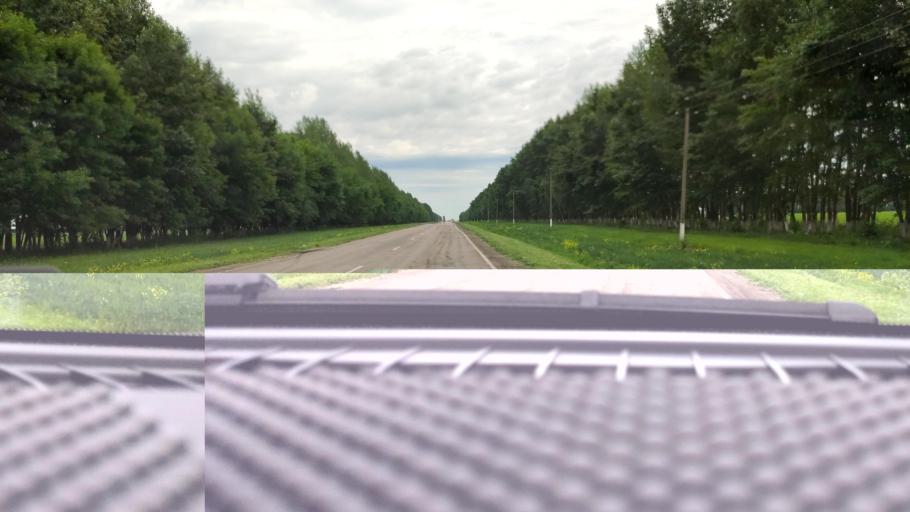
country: RU
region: Voronezj
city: Panino
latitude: 51.6539
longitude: 40.0767
